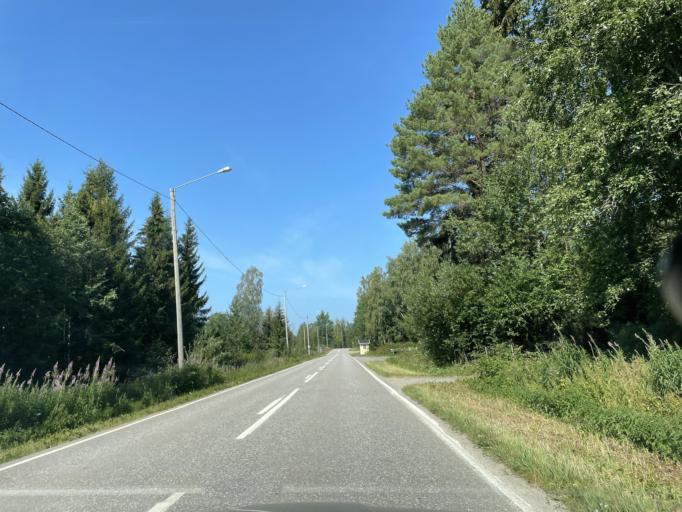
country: FI
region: Central Finland
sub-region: Saarijaervi-Viitasaari
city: Pihtipudas
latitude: 63.3573
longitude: 25.7541
